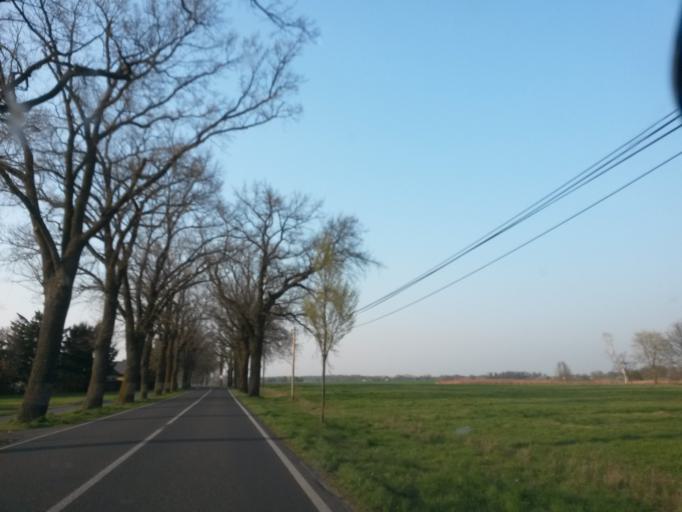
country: DE
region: Brandenburg
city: Rehfelde
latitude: 52.5095
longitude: 13.9304
